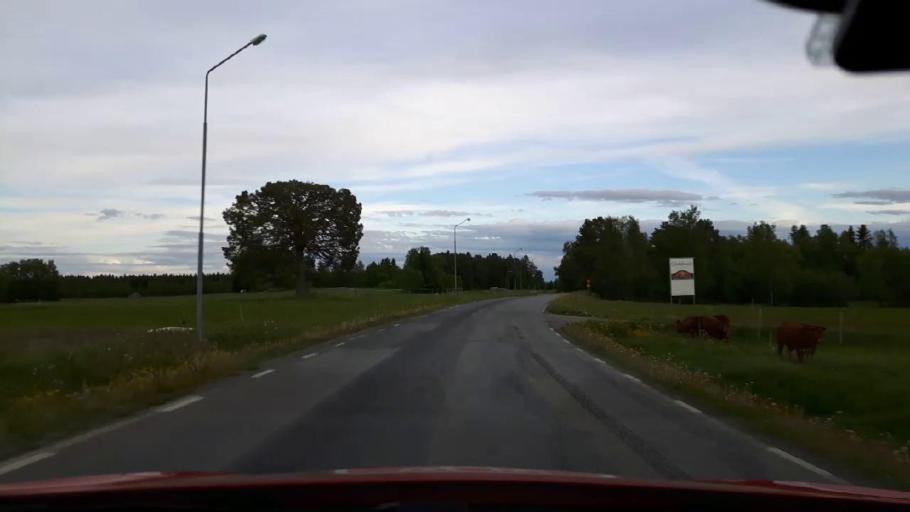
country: SE
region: Jaemtland
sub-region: OEstersunds Kommun
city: Ostersund
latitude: 63.0569
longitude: 14.4507
